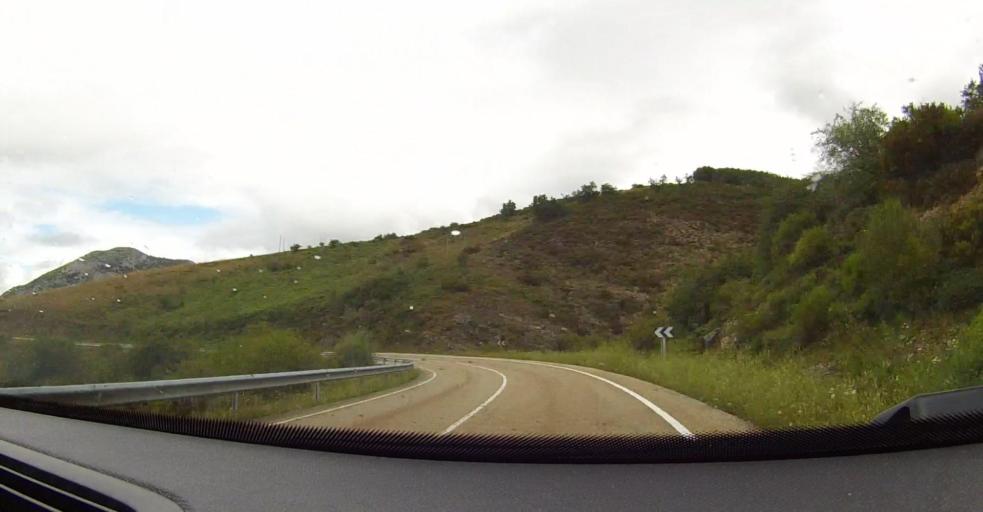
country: ES
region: Castille and Leon
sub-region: Provincia de Leon
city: Puebla de Lillo
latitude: 42.9363
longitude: -5.2719
